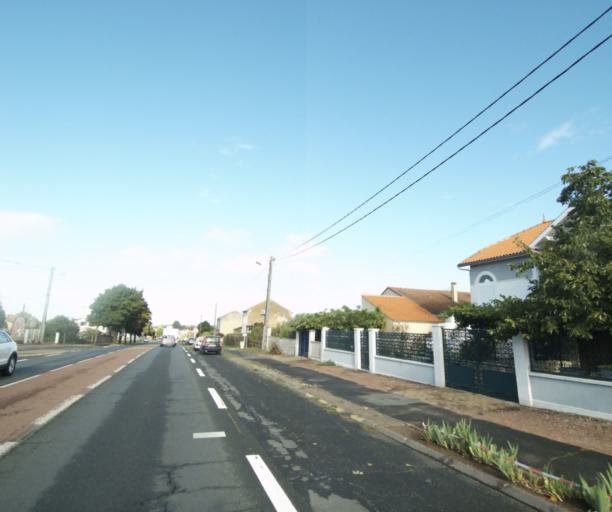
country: FR
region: Poitou-Charentes
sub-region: Departement de la Charente-Maritime
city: Tonnay-Charente
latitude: 45.9486
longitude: -0.9157
